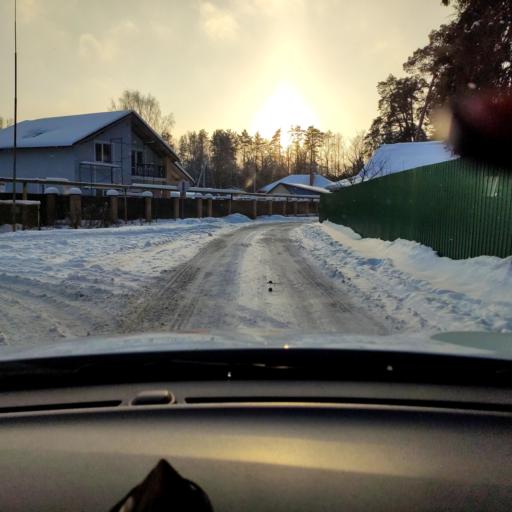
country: RU
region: Tatarstan
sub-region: Zelenodol'skiy Rayon
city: Vasil'yevo
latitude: 55.9093
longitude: 48.7473
